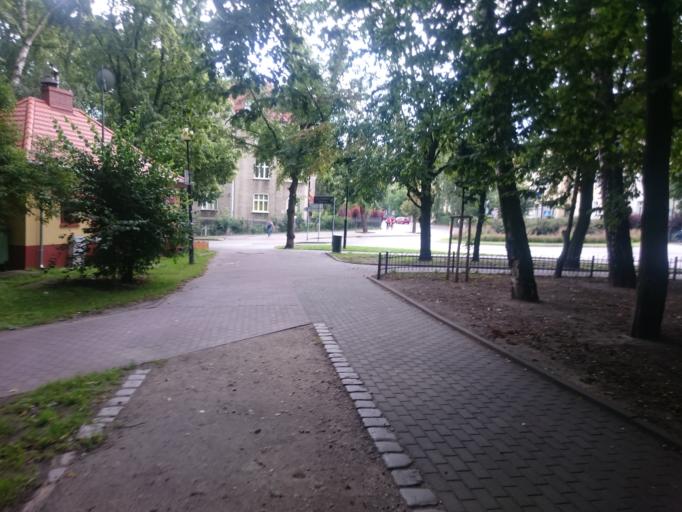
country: PL
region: Pomeranian Voivodeship
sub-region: Sopot
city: Sopot
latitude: 54.4422
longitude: 18.5569
